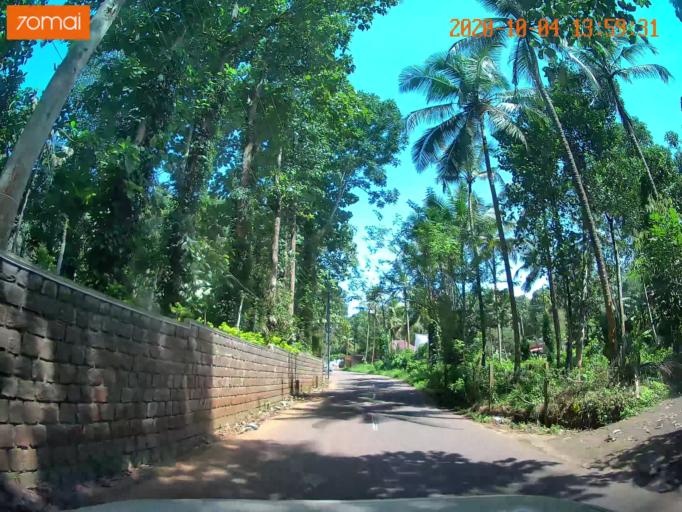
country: IN
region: Kerala
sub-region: Kottayam
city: Lalam
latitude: 9.7169
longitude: 76.6632
